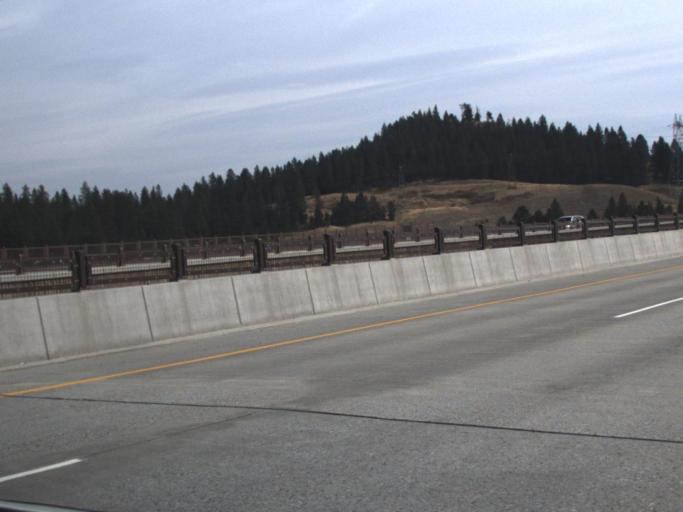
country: US
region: Washington
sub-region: Spokane County
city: Mead
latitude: 47.7570
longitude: -117.3634
